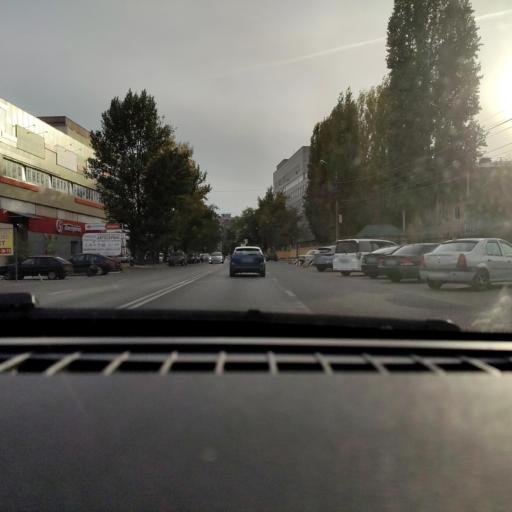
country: RU
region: Voronezj
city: Voronezh
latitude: 51.6767
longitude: 39.2513
